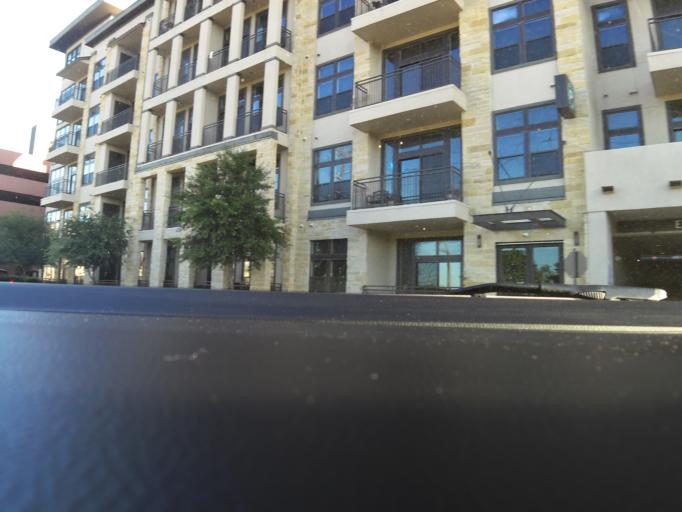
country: US
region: Texas
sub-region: Harris County
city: Bellaire
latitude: 29.7332
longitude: -95.4618
